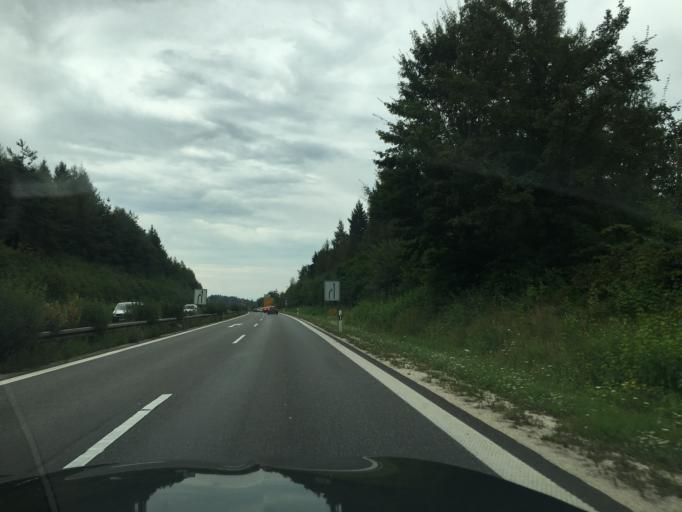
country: DE
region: Baden-Wuerttemberg
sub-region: Freiburg Region
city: Radolfzell am Bodensee
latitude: 47.7362
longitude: 9.0218
